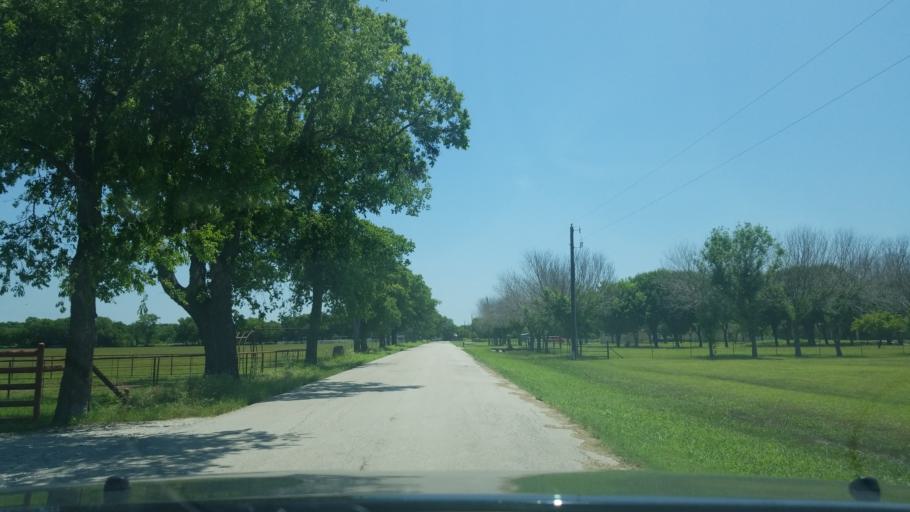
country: US
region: Texas
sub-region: Denton County
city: Sanger
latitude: 33.3419
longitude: -97.2248
